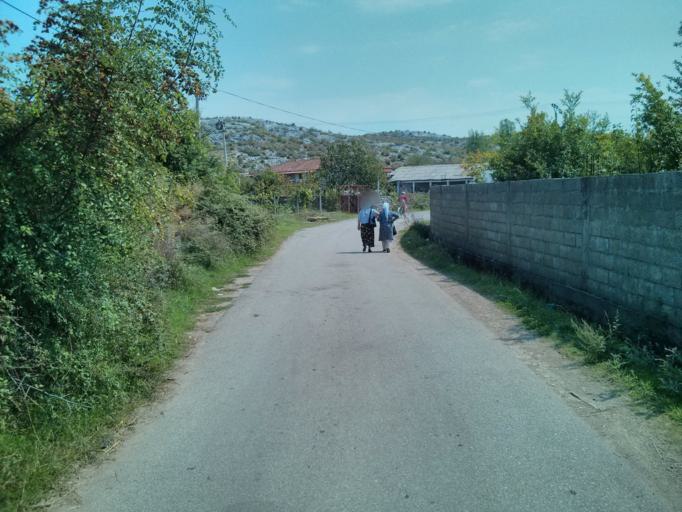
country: AL
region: Shkoder
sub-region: Rrethi i Malesia e Madhe
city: Gruemire
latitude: 42.1329
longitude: 19.5517
